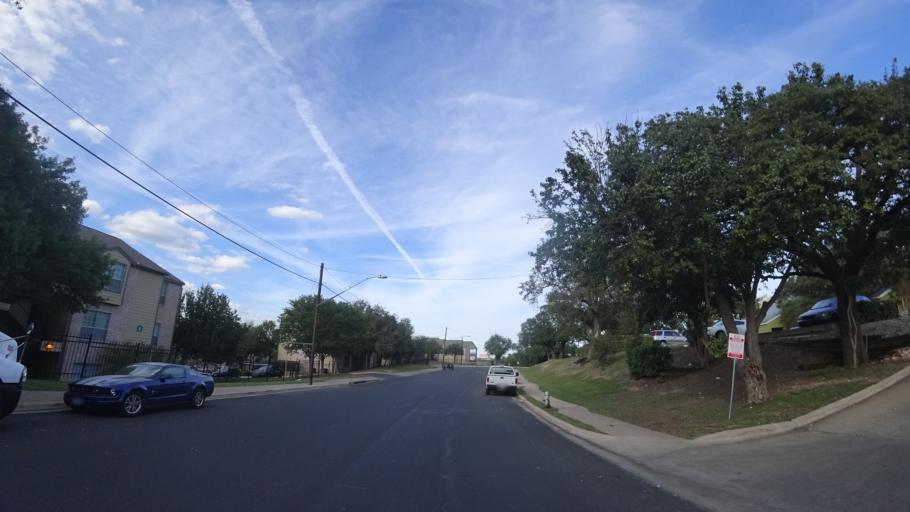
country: US
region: Texas
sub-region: Travis County
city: Onion Creek
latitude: 30.1938
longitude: -97.7642
